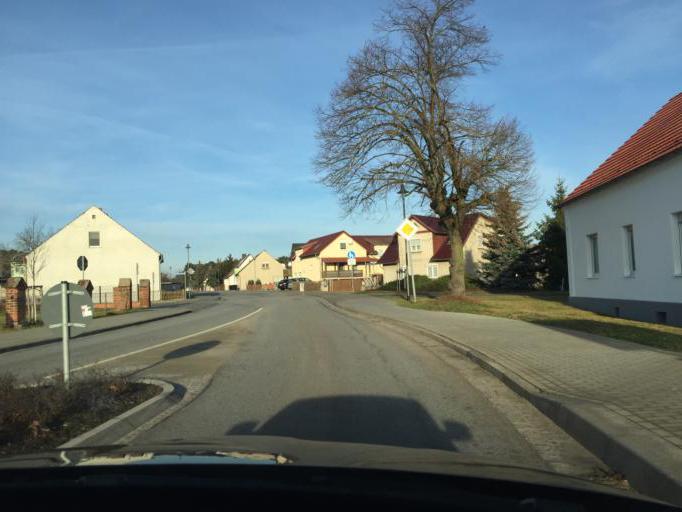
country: DE
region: Brandenburg
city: Ziltendorf
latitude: 52.2064
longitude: 14.6242
